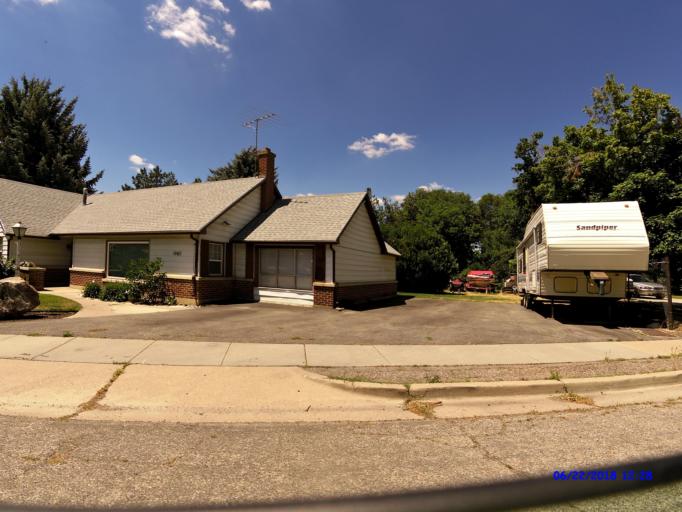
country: US
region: Utah
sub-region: Weber County
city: Ogden
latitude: 41.2400
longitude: -111.9607
